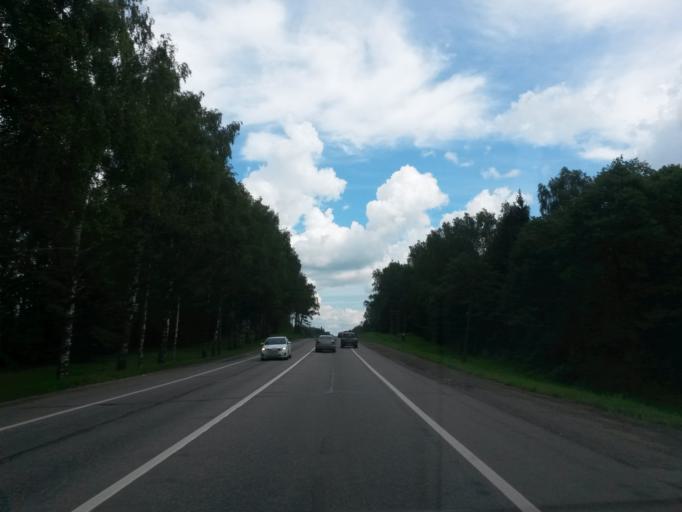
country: RU
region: Vladimir
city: Balakirevo
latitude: 56.6285
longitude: 38.6665
